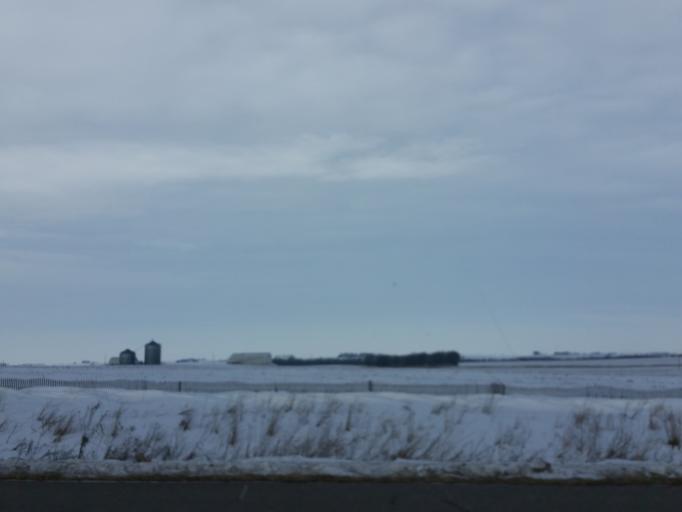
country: US
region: Iowa
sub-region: Delaware County
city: Manchester
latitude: 42.4646
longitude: -91.6029
